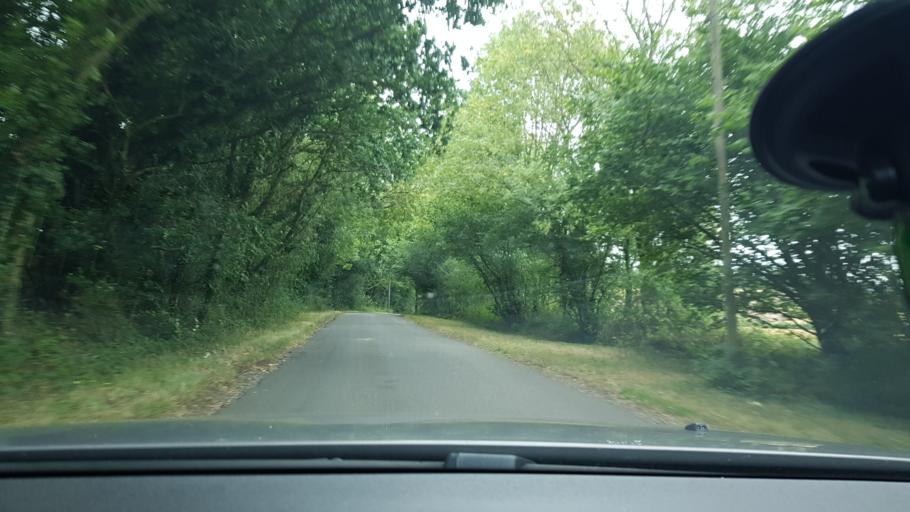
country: GB
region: England
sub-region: Wiltshire
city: Chilton Foliat
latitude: 51.4674
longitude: -1.5505
